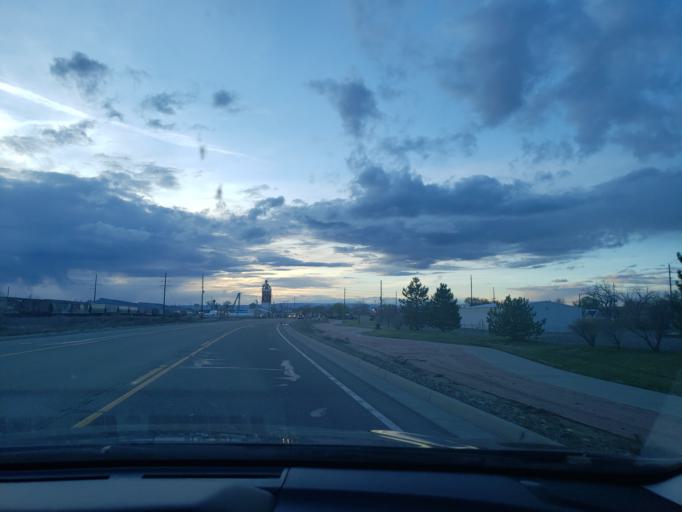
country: US
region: Colorado
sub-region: Mesa County
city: Fruita
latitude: 39.1523
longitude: -108.7270
